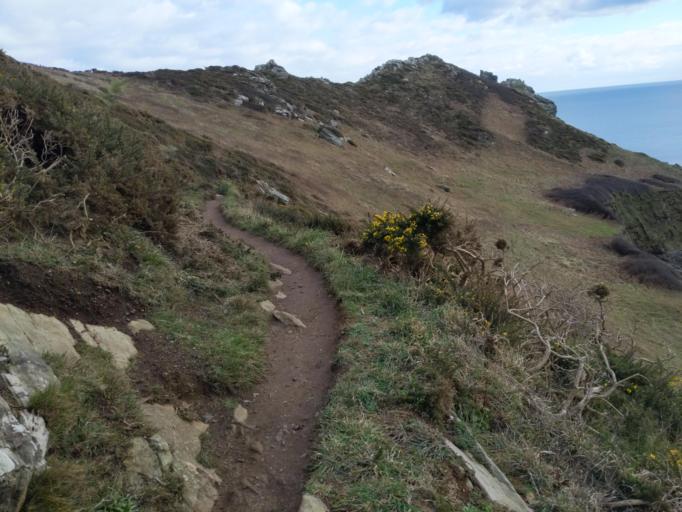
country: GB
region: England
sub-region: Devon
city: Salcombe
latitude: 50.2105
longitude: -3.7321
